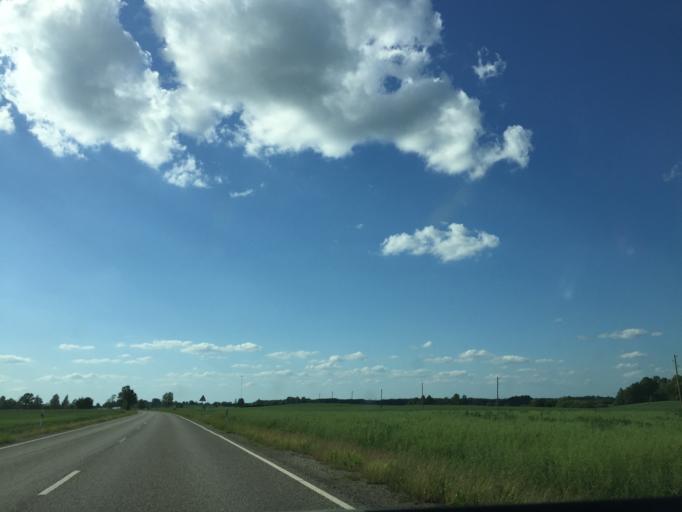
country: LV
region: Kandava
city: Kandava
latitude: 56.9122
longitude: 22.8341
